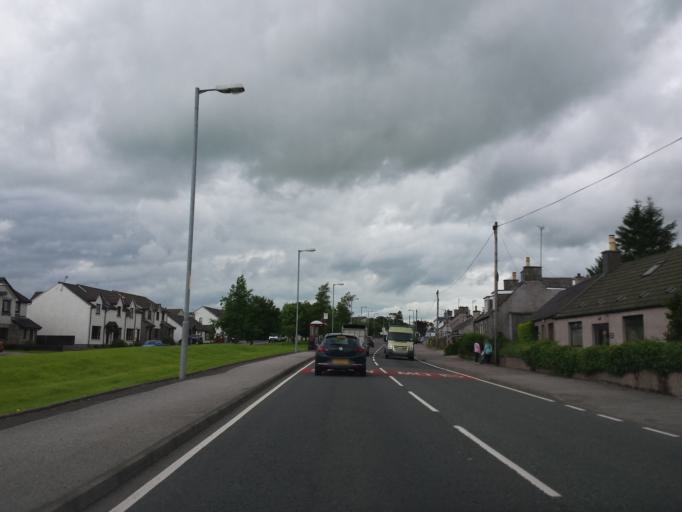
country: GB
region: Scotland
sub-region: Dumfries and Galloway
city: Dalbeattie
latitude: 55.0112
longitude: -3.8672
